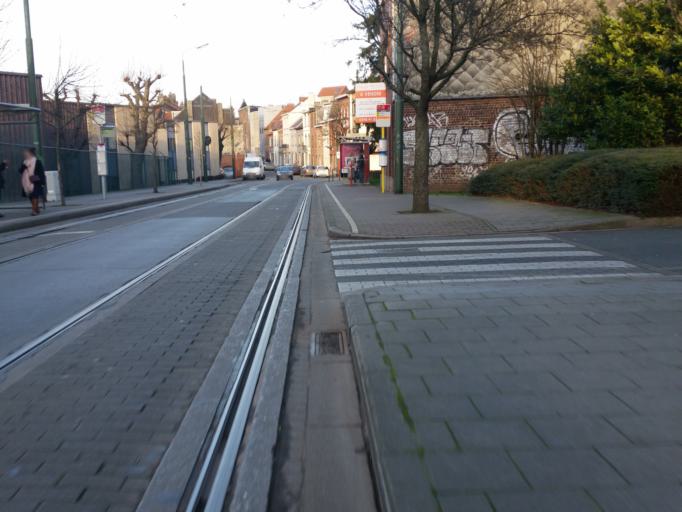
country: BE
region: Flanders
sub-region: Provincie Vlaams-Brabant
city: Diegem
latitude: 50.8787
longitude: 4.4037
